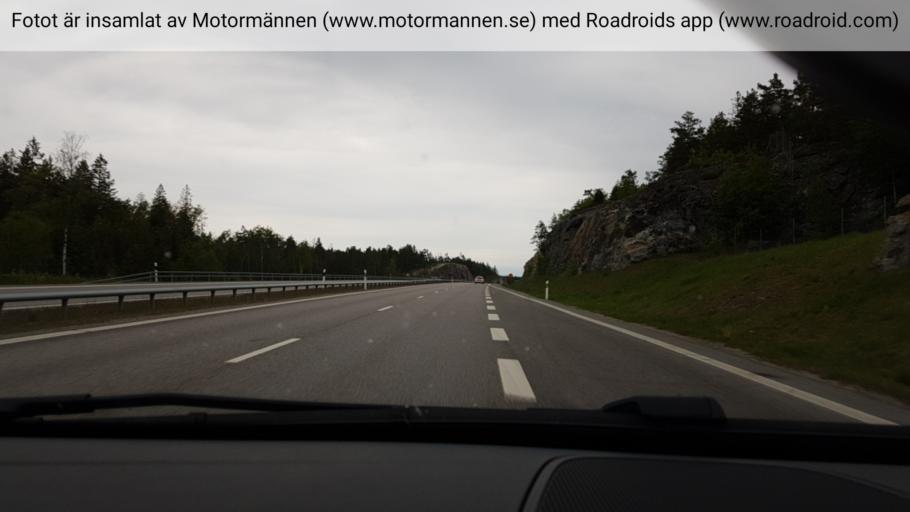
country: SE
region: Stockholm
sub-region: Nynashamns Kommun
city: Osmo
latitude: 59.0304
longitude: 17.9551
